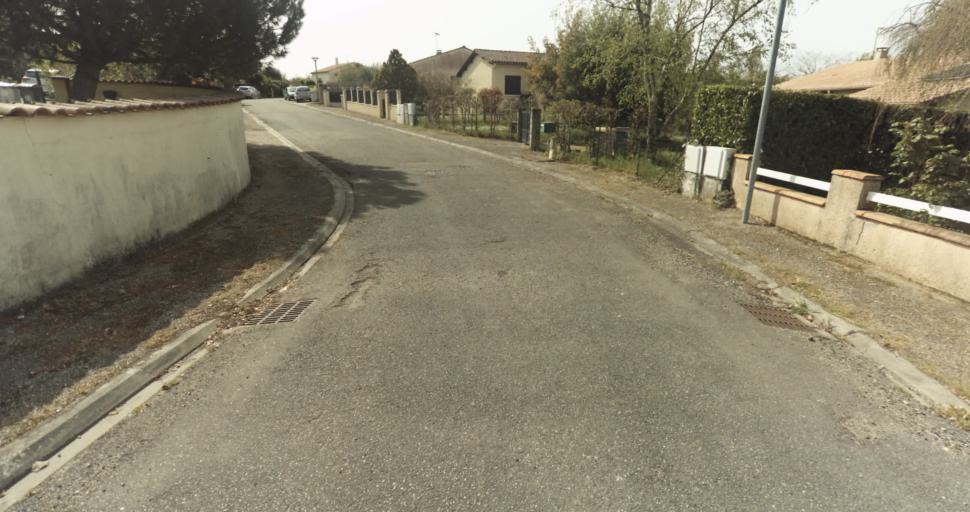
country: FR
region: Midi-Pyrenees
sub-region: Departement du Tarn-et-Garonne
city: Moissac
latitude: 44.1152
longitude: 1.0737
